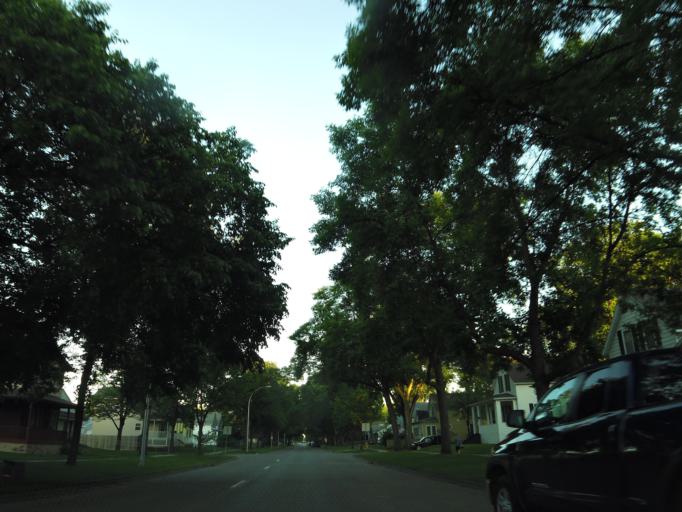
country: US
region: North Dakota
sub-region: Grand Forks County
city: Grand Forks
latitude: 47.9306
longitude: -97.0422
